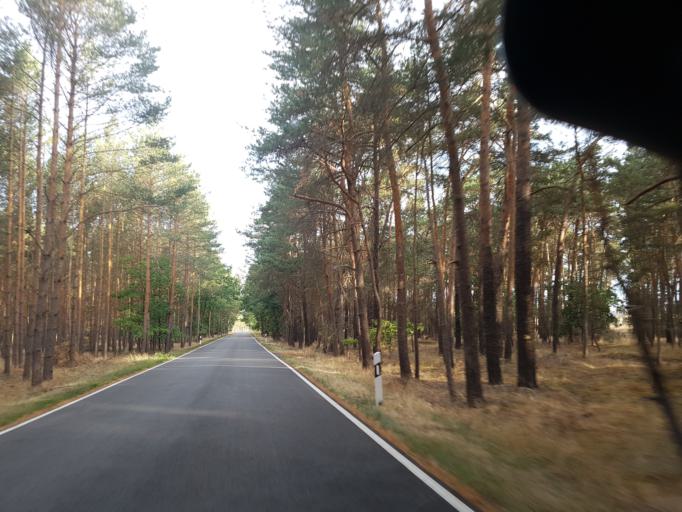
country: DE
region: Saxony-Anhalt
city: Holzdorf
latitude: 51.7987
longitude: 13.0939
